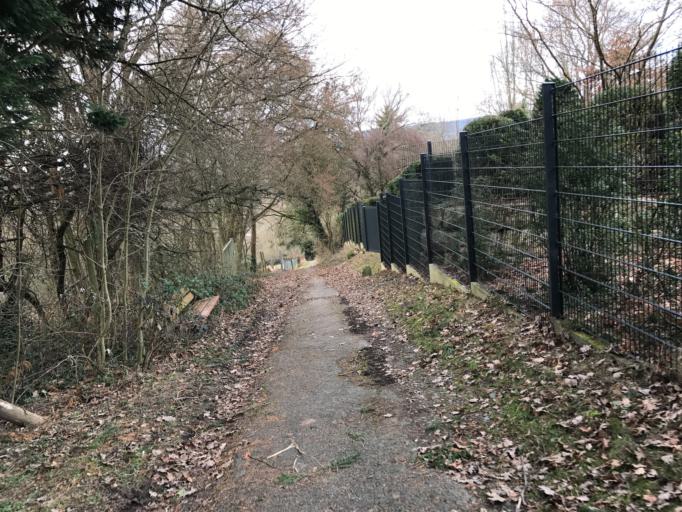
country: DE
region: Hesse
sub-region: Regierungsbezirk Darmstadt
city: Wiesbaden
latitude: 50.0989
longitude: 8.2701
